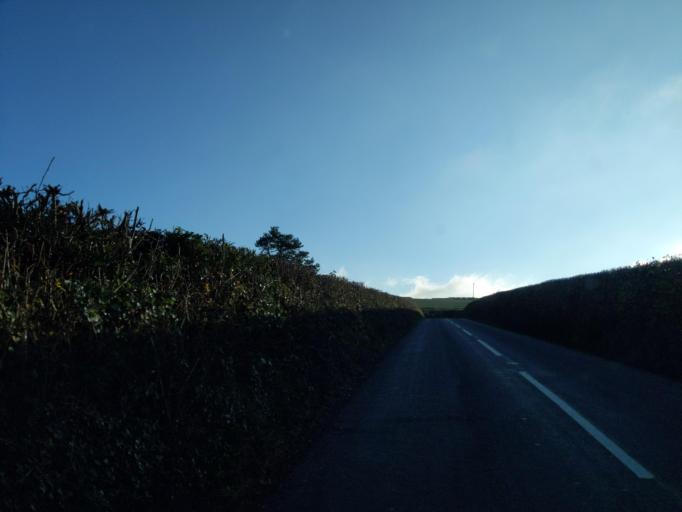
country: GB
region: England
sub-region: Cornwall
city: Pillaton
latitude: 50.4075
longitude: -4.3315
